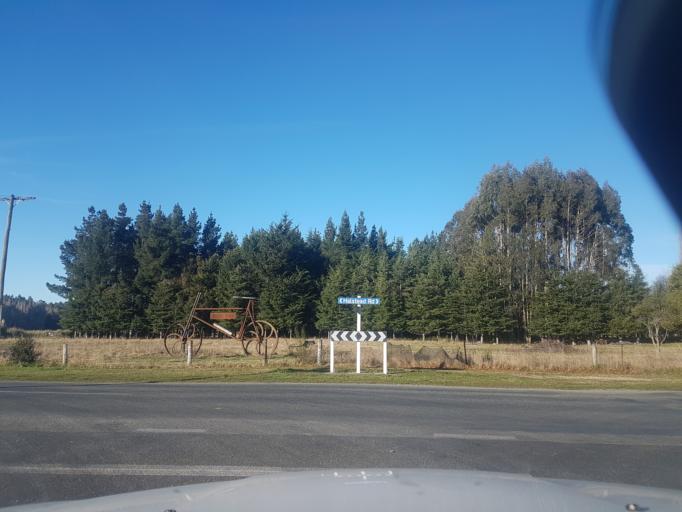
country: NZ
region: Canterbury
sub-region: Timaru District
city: Pleasant Point
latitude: -44.2561
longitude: 171.1318
